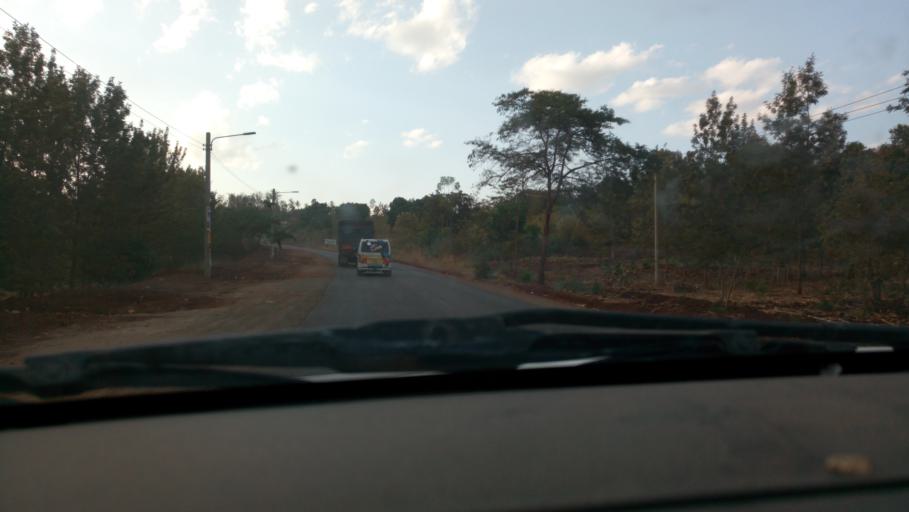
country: KE
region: Murang'a District
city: Murang'a
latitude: -0.7430
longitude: 37.1635
